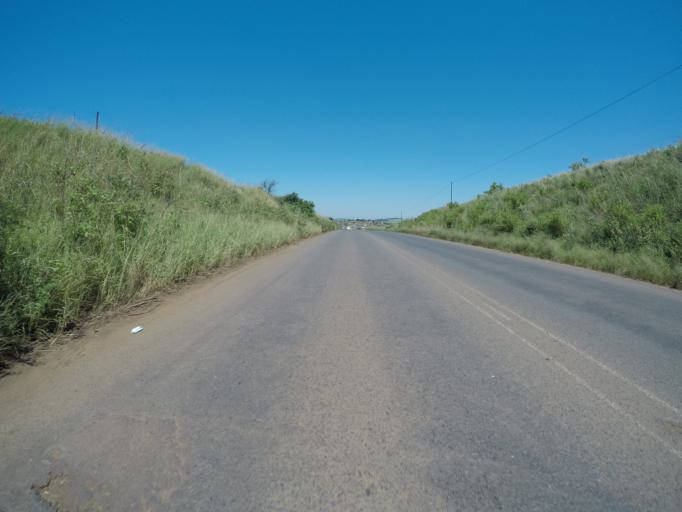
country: ZA
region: KwaZulu-Natal
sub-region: uThungulu District Municipality
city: Empangeni
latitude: -28.7617
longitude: 31.8750
